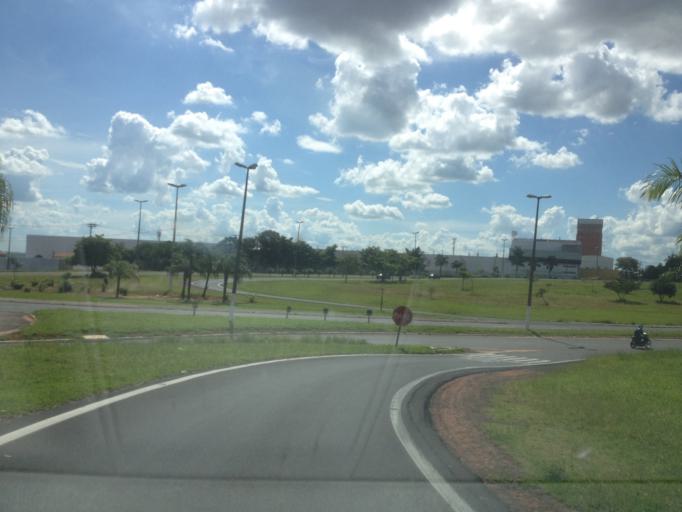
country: BR
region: Sao Paulo
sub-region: Marilia
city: Marilia
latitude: -22.2333
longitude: -49.9290
